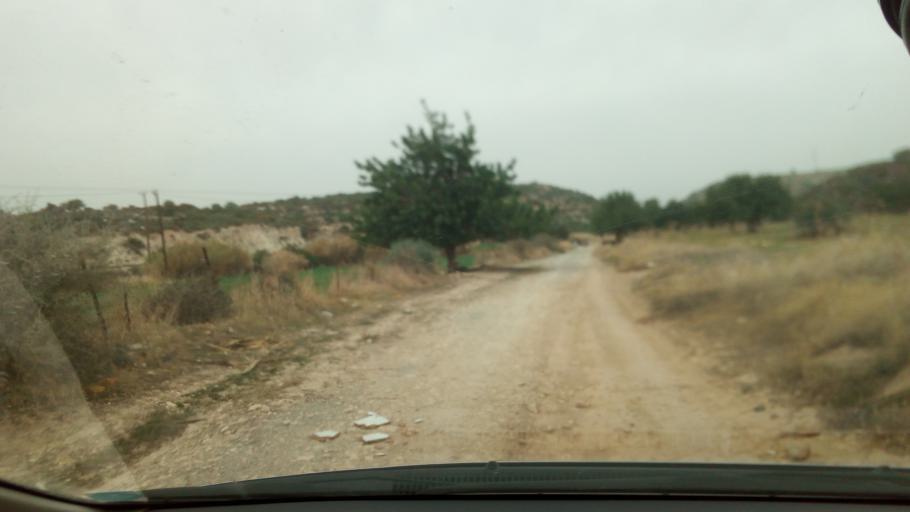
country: CY
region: Limassol
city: Ypsonas
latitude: 34.7090
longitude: 32.9563
